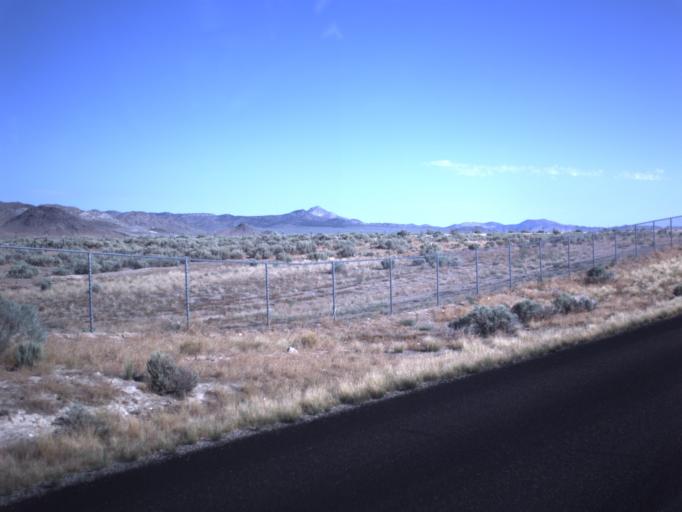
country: US
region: Utah
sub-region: Beaver County
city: Milford
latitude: 38.4313
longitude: -113.0097
